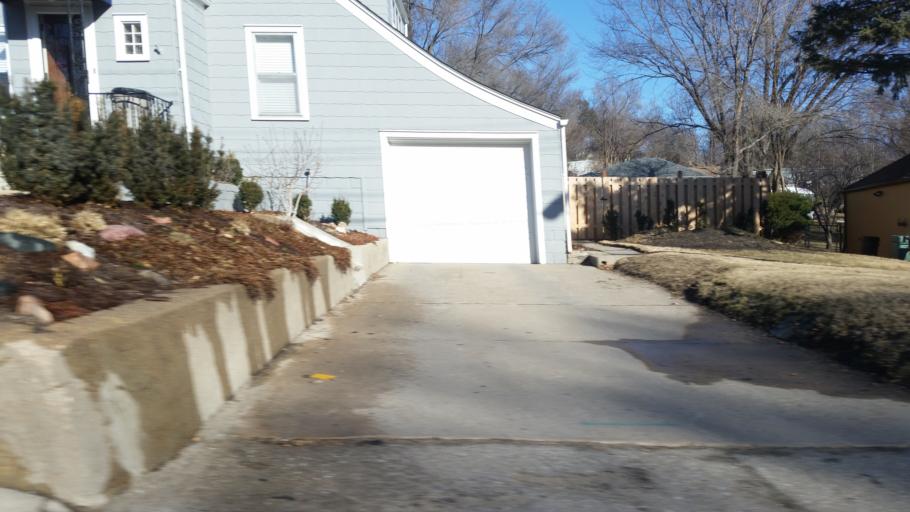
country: US
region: Nebraska
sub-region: Sarpy County
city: Bellevue
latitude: 41.1897
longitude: -95.9334
